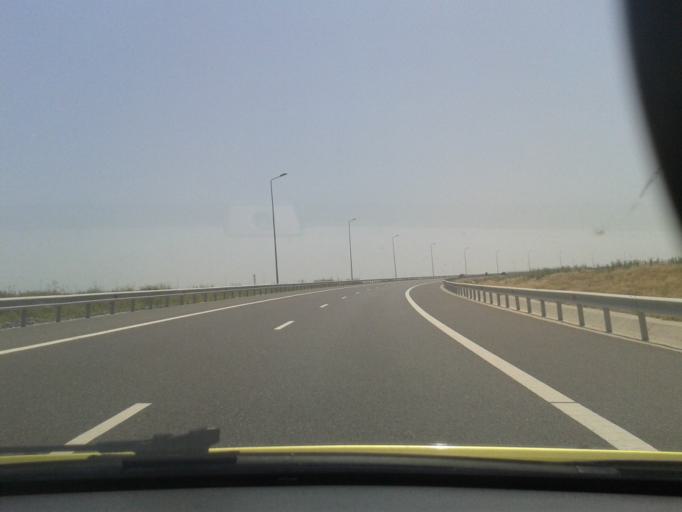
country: RO
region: Constanta
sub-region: Comuna Cumpana
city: Cumpana
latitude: 44.1501
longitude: 28.5537
